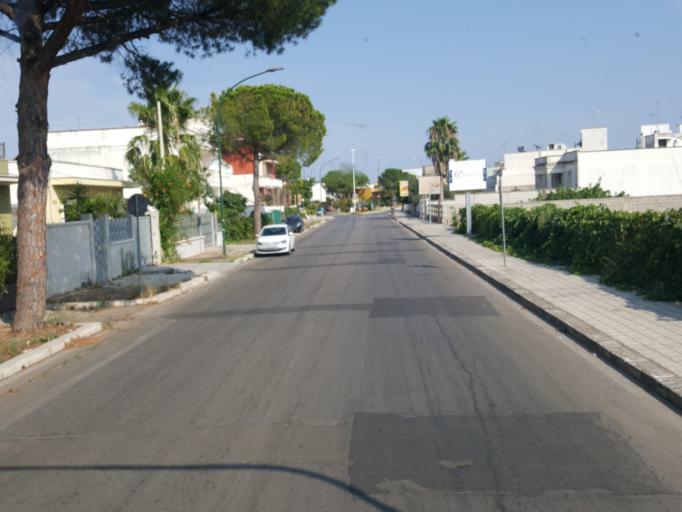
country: IT
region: Apulia
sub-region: Provincia di Lecce
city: Campi Salentina
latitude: 40.4025
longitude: 18.0197
